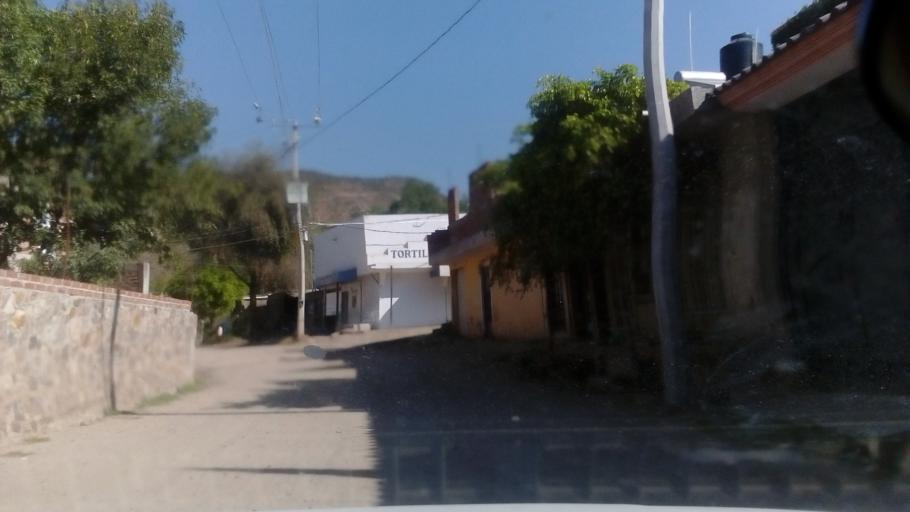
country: MX
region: Guanajuato
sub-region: Leon
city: Medina
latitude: 21.1492
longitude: -101.6075
